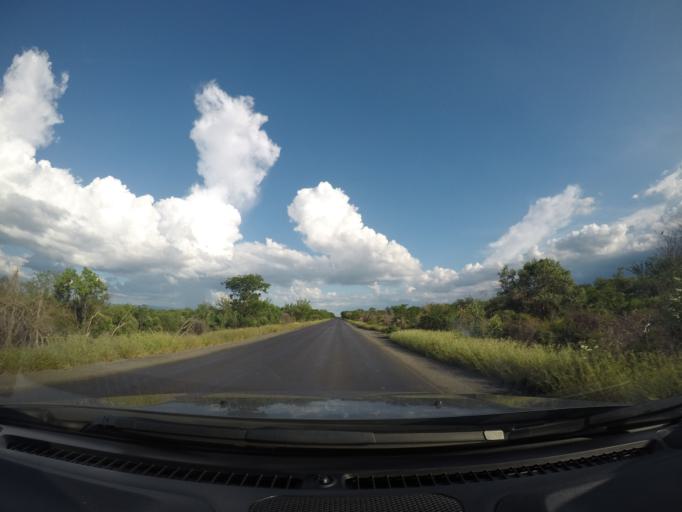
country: BR
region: Bahia
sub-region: Oliveira Dos Brejinhos
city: Oliveira dos Brejinhos
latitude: -12.0875
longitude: -42.9348
